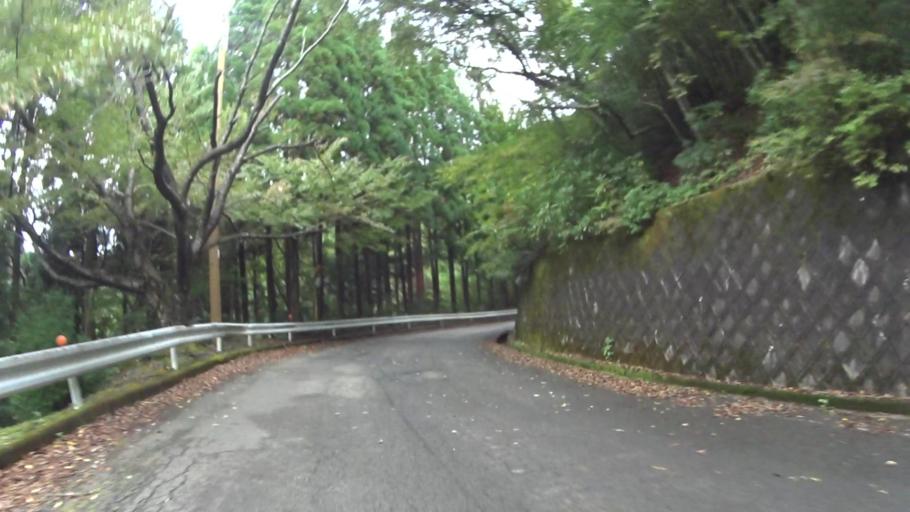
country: JP
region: Shiga Prefecture
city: Kitahama
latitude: 35.2692
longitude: 135.7412
